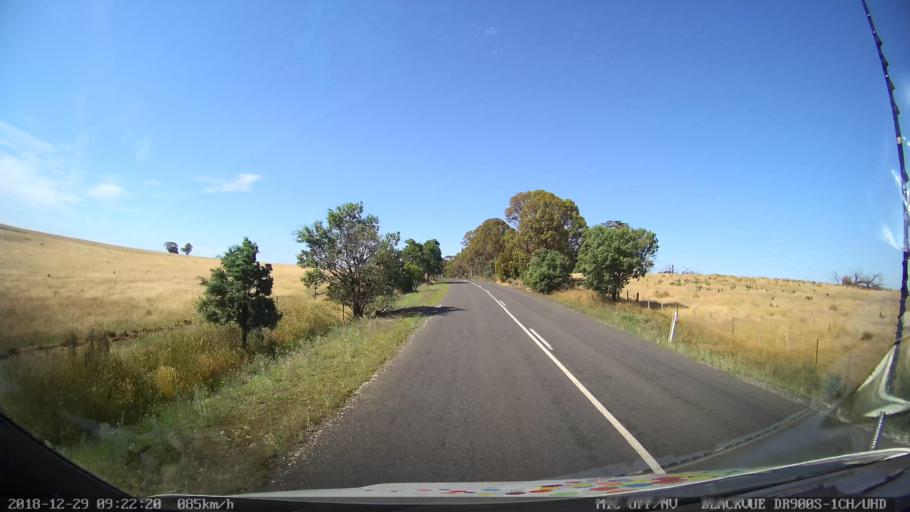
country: AU
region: New South Wales
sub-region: Upper Lachlan Shire
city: Crookwell
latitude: -34.5112
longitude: 149.4067
